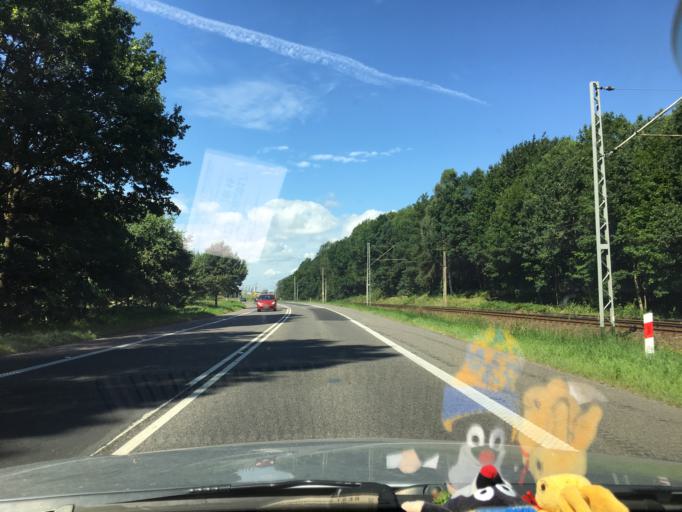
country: PL
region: West Pomeranian Voivodeship
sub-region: Powiat kamienski
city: Wolin
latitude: 53.8464
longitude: 14.6929
